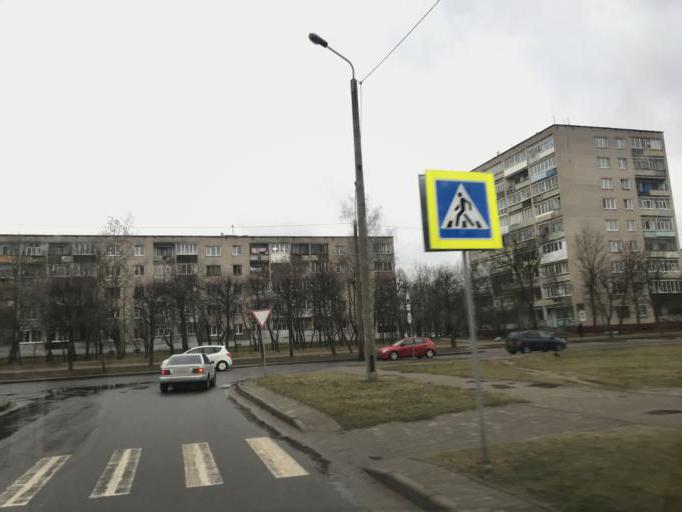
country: BY
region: Mogilev
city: Mahilyow
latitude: 53.8784
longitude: 30.3259
